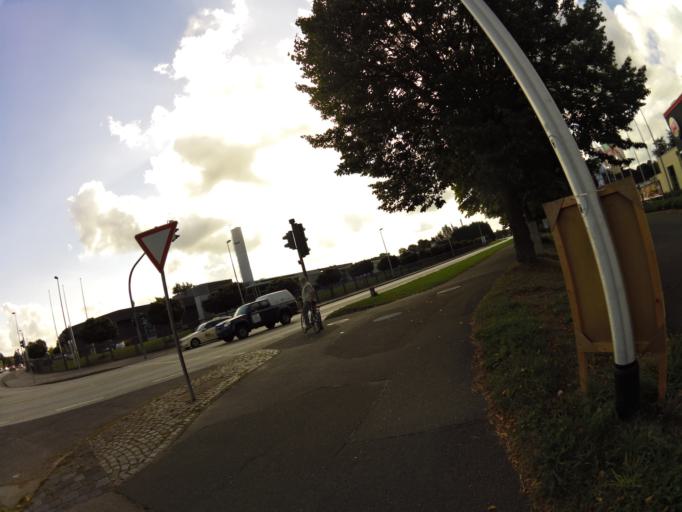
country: DE
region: Schleswig-Holstein
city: Eckernforde
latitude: 54.4511
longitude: 9.8308
